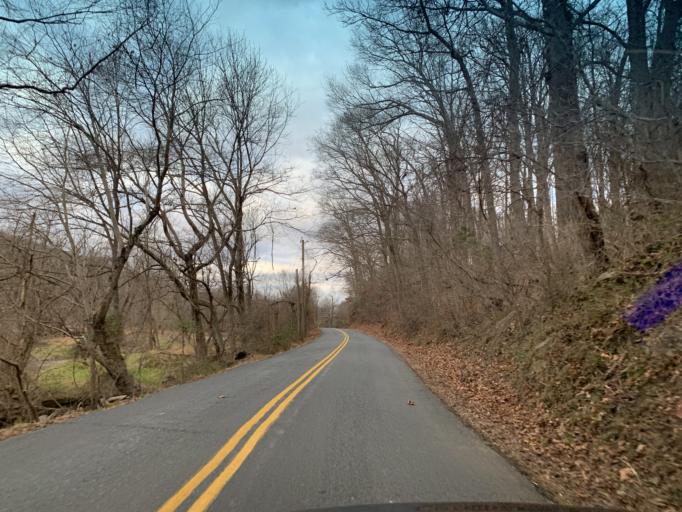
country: US
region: Maryland
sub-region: Harford County
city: Jarrettsville
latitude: 39.6463
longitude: -76.4293
